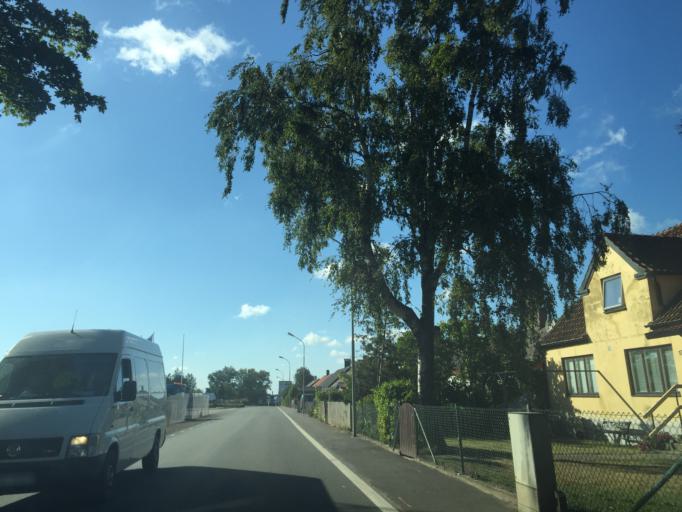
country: SE
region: Skane
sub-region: Ystads Kommun
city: Kopingebro
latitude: 55.4495
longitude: 14.0233
